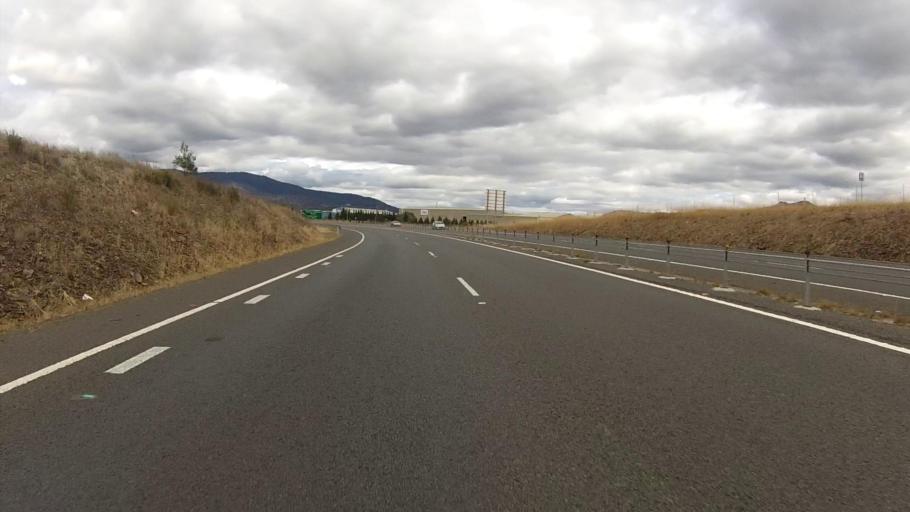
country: AU
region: Tasmania
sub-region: Brighton
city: Bridgewater
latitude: -42.7166
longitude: 147.2406
